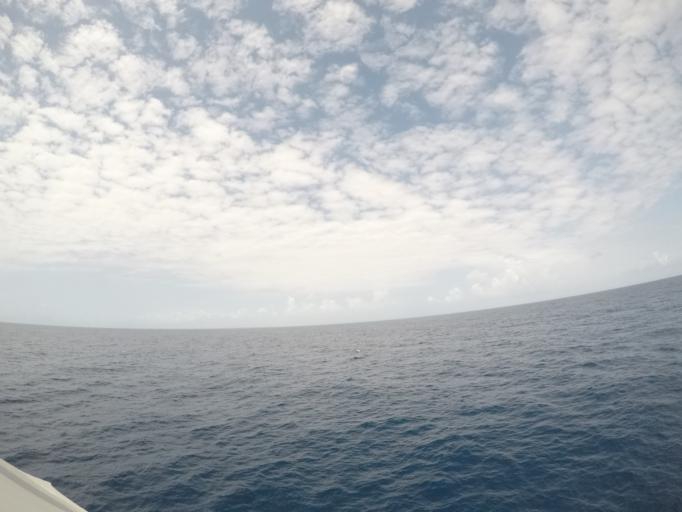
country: TZ
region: Zanzibar North
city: Nungwi
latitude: -5.5851
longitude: 39.3549
